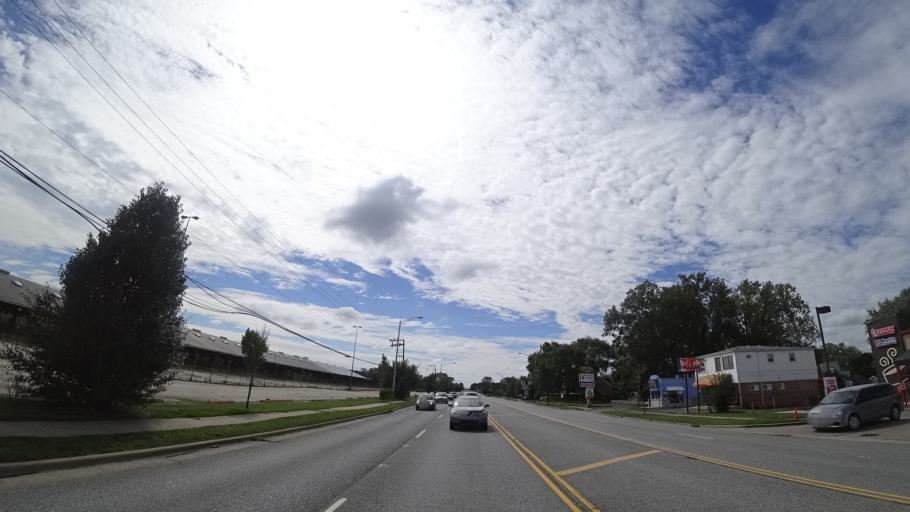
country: US
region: Illinois
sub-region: Cook County
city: Worth
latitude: 41.7031
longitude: -87.7979
